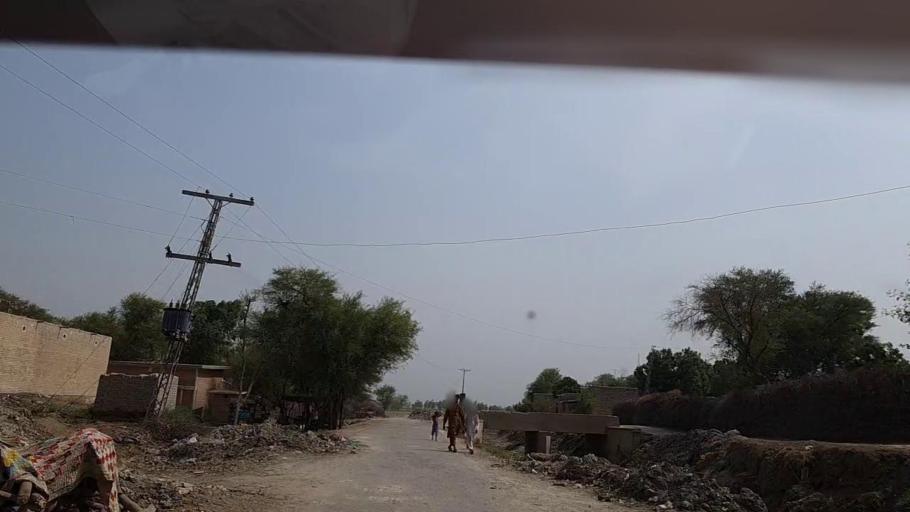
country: PK
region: Sindh
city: Khairpur Nathan Shah
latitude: 27.0647
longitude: 67.6875
